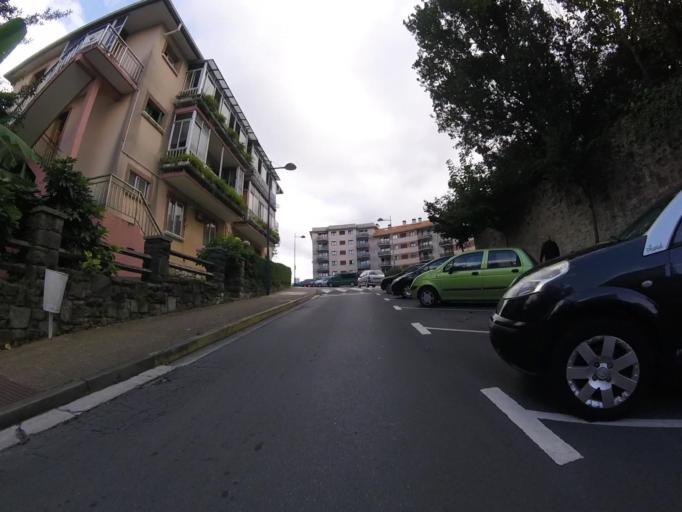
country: ES
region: Basque Country
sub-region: Provincia de Guipuzcoa
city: Errenteria
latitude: 43.3072
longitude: -1.8950
